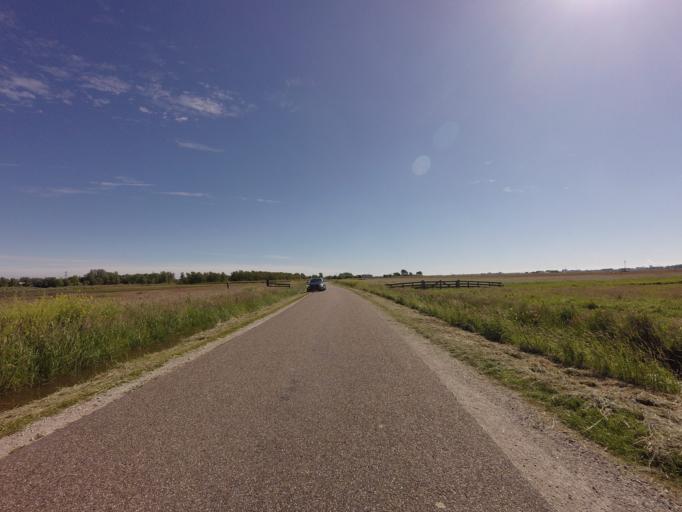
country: NL
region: North Holland
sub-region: Gemeente Uitgeest
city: Uitgeest
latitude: 52.5227
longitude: 4.7476
